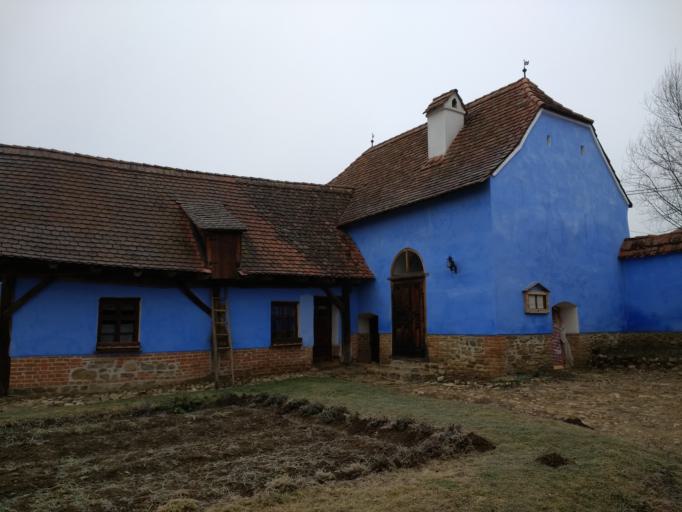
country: RO
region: Brasov
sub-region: Oras Rupea
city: Fiser
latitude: 46.0563
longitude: 25.0971
